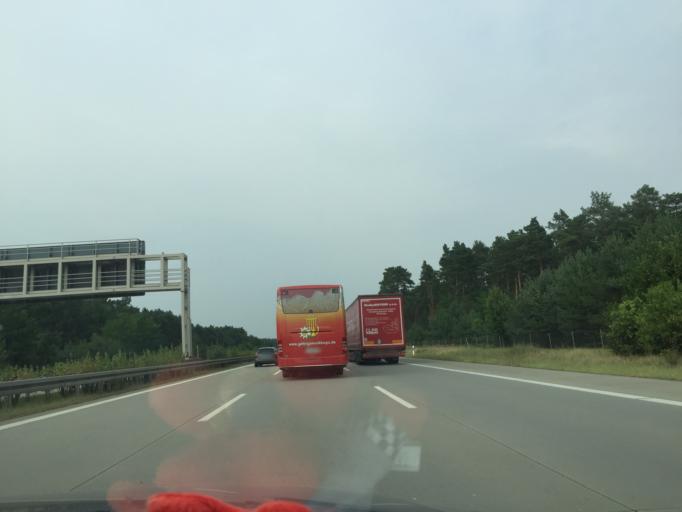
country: DE
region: Brandenburg
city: Erkner
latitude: 52.3408
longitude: 13.7544
